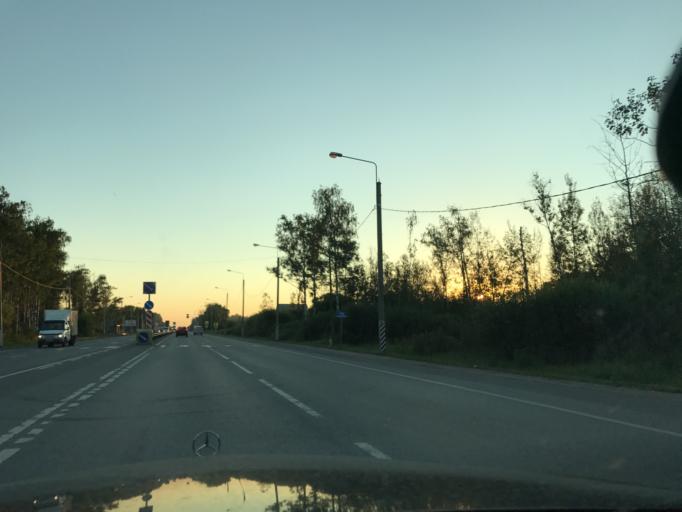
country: RU
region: Vladimir
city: Petushki
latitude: 55.9332
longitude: 39.3969
